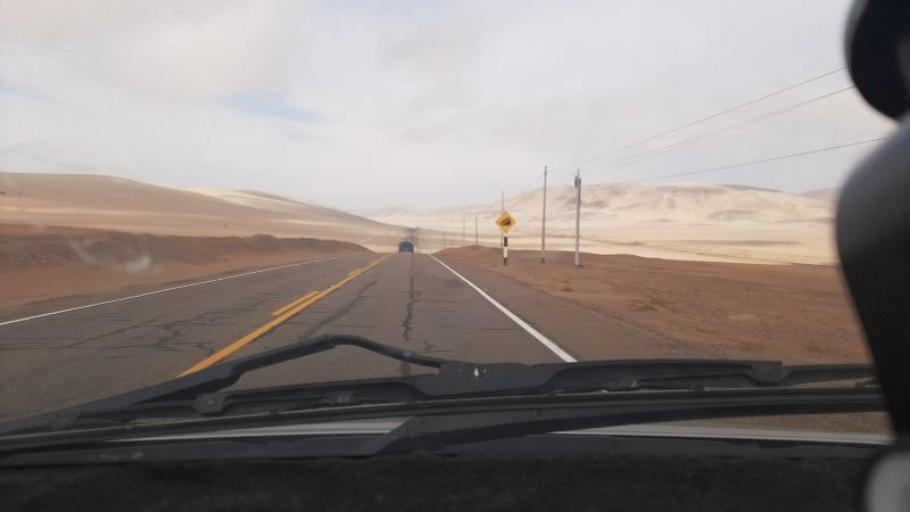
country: PE
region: Moquegua
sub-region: Provincia de Ilo
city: El Algarrobal
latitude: -17.6919
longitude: -71.2432
